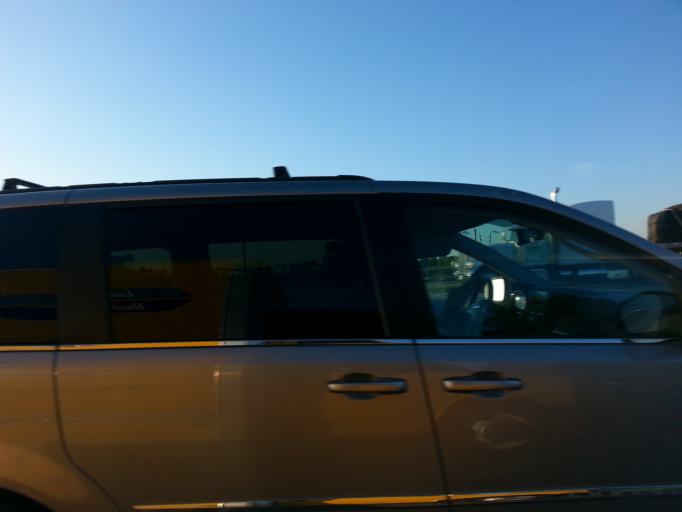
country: US
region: Illinois
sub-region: Vermilion County
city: Danville
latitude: 40.1156
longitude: -87.5463
